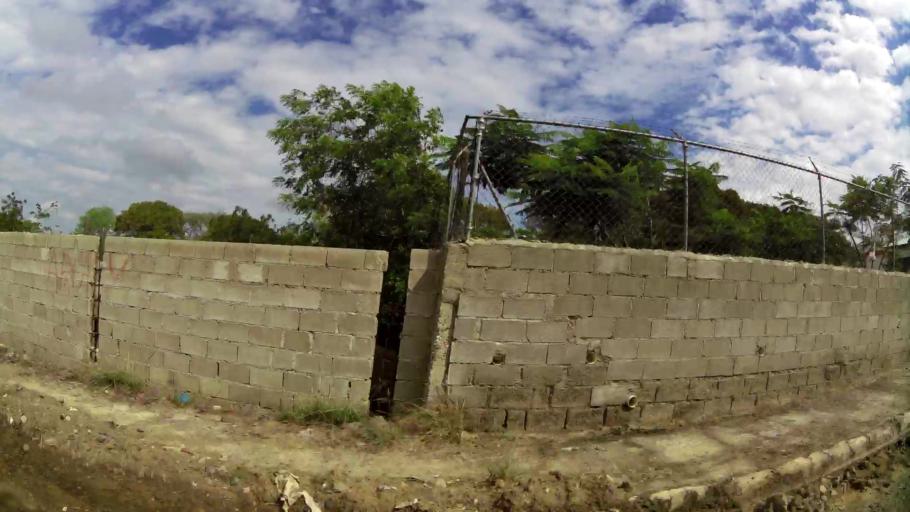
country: DO
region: Santiago
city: Palmar Arriba
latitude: 19.4908
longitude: -70.7282
